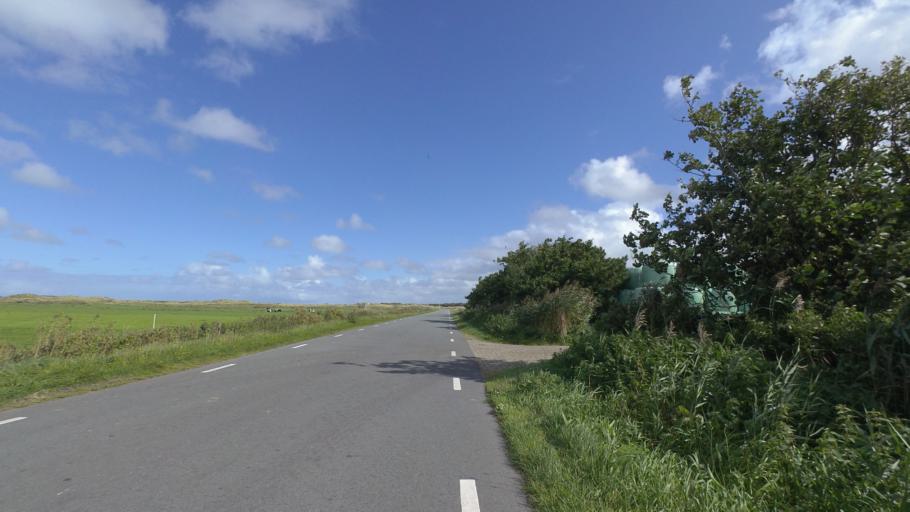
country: NL
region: Friesland
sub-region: Gemeente Ameland
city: Nes
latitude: 53.4501
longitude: 5.8270
